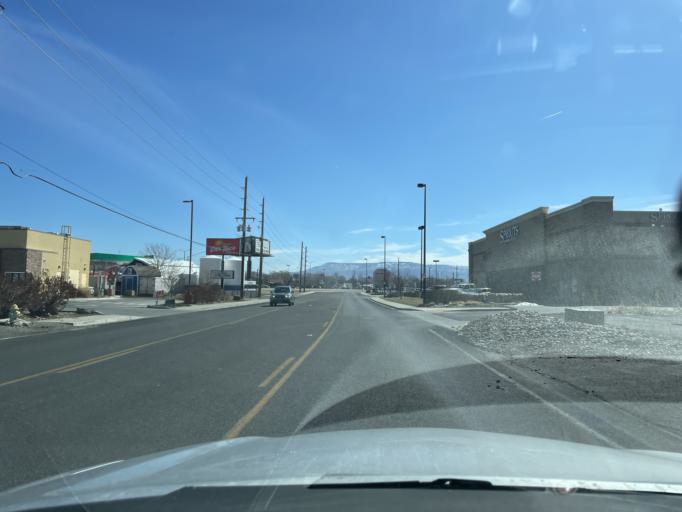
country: US
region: Colorado
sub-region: Mesa County
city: Grand Junction
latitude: 39.0810
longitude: -108.5874
